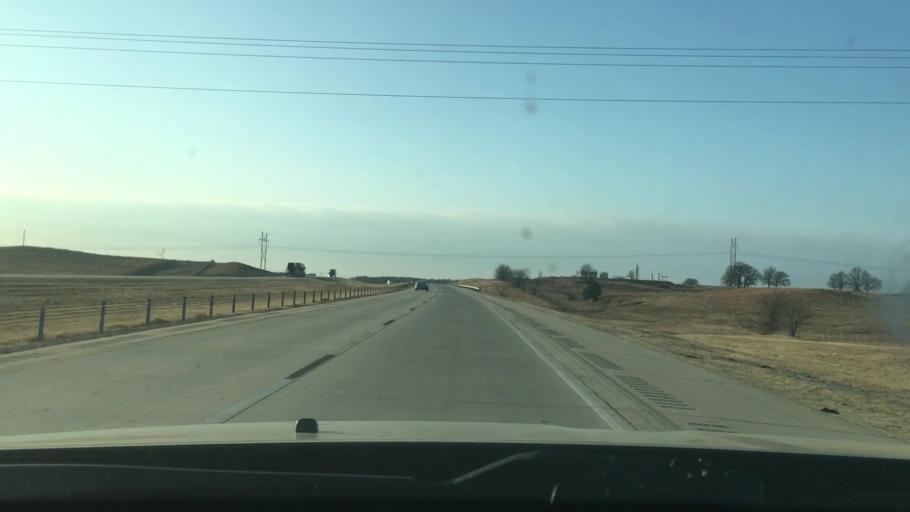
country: US
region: Oklahoma
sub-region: Carter County
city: Ardmore
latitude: 34.2567
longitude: -97.1653
